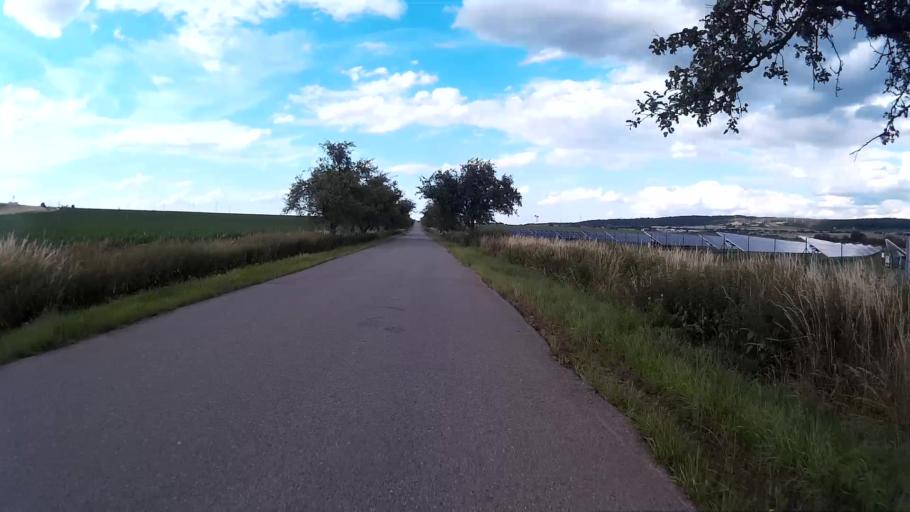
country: CZ
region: South Moravian
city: Ricany
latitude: 49.1981
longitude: 16.4001
